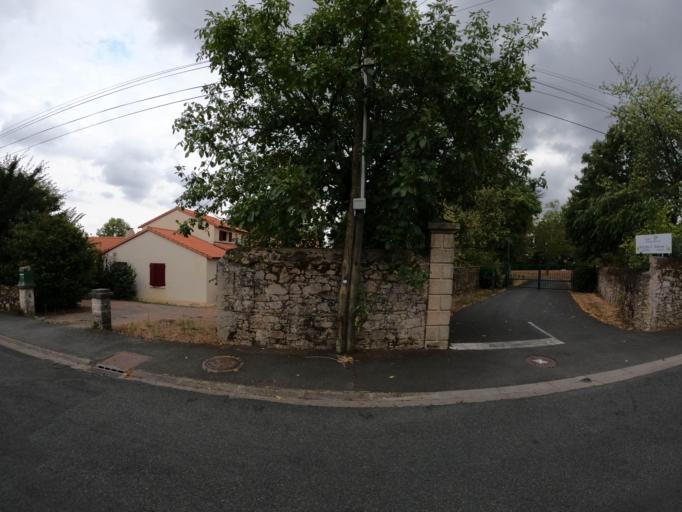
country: FR
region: Pays de la Loire
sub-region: Departement de Maine-et-Loire
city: Le Longeron
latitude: 47.0172
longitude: -1.0646
